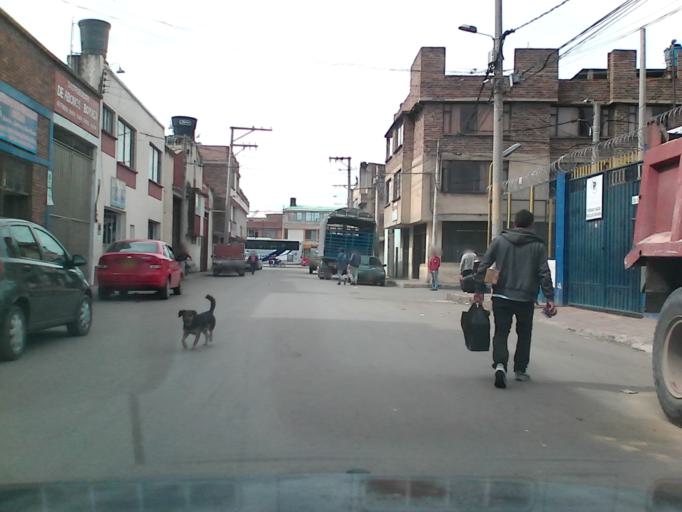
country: CO
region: Boyaca
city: Sogamoso
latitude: 5.7192
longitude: -72.9346
